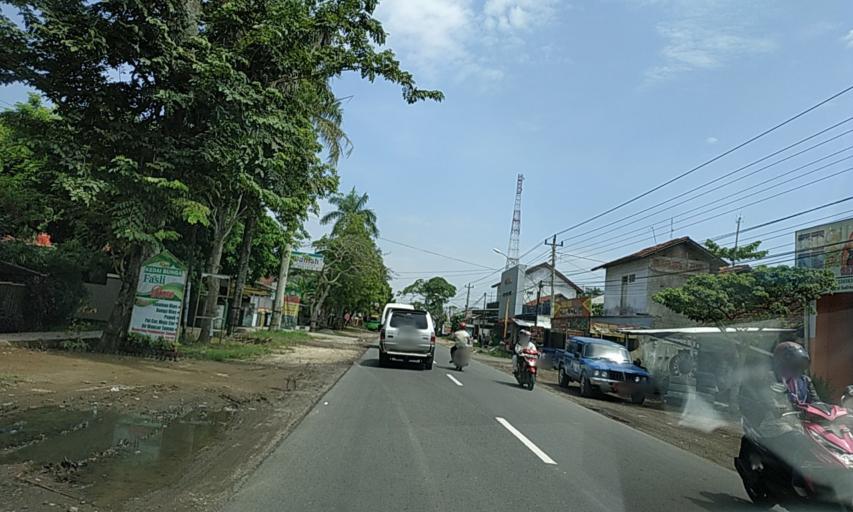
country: ID
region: Central Java
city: Sidareja
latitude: -7.4856
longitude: 108.7983
